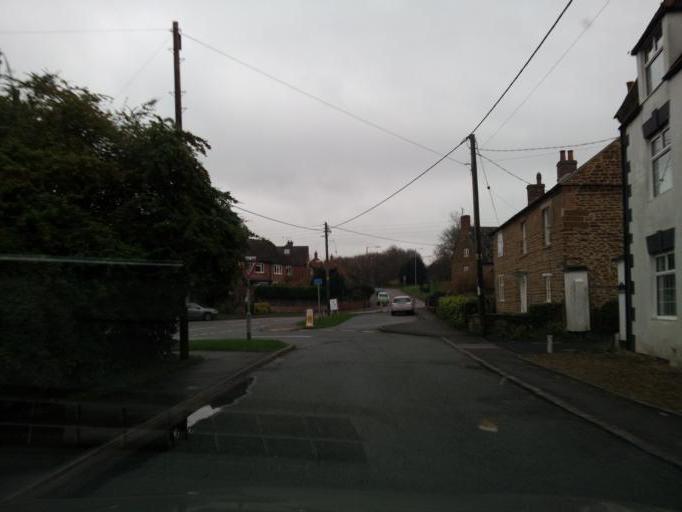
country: GB
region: England
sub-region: Northamptonshire
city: Daventry
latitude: 52.3339
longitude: -1.1770
